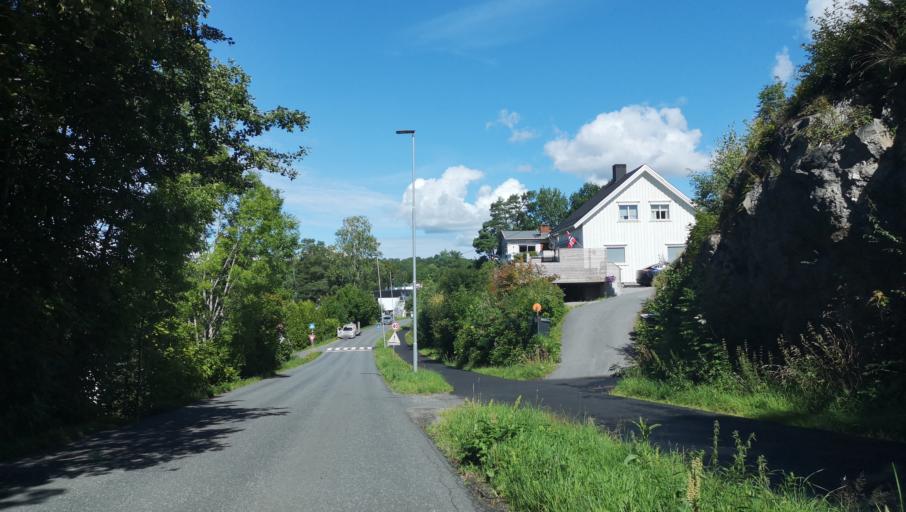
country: NO
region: Akershus
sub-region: Frogn
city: Drobak
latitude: 59.6627
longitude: 10.6404
